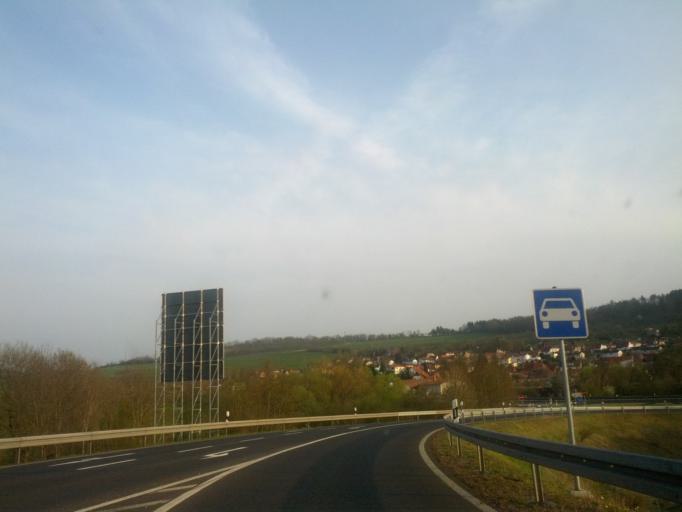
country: DE
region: Thuringia
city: Eisenach
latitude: 50.9805
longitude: 10.3602
